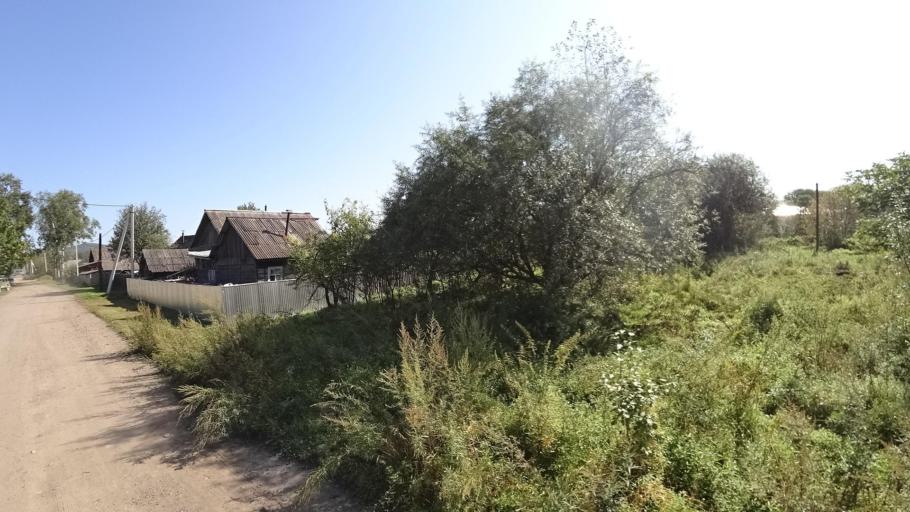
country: RU
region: Jewish Autonomous Oblast
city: Bira
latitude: 48.9927
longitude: 132.4642
